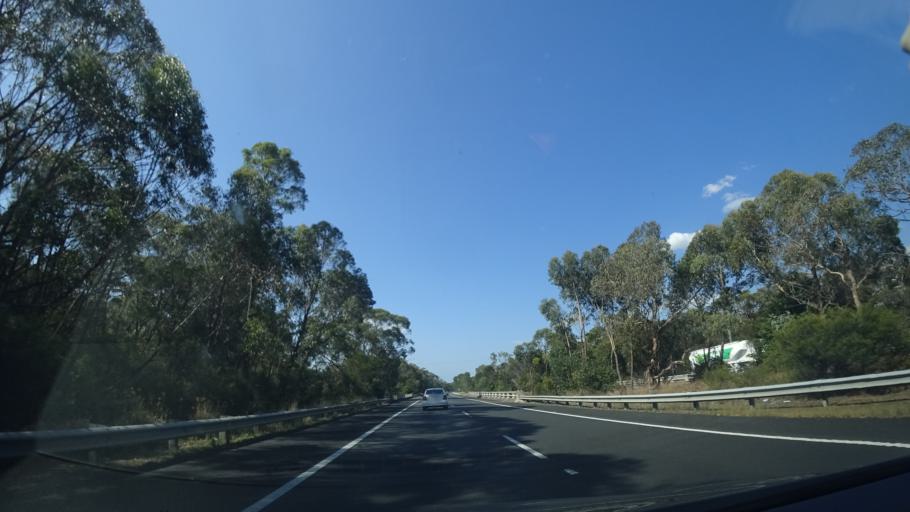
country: AU
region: New South Wales
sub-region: Wollondilly
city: Buxton
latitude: -34.3376
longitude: 150.5568
